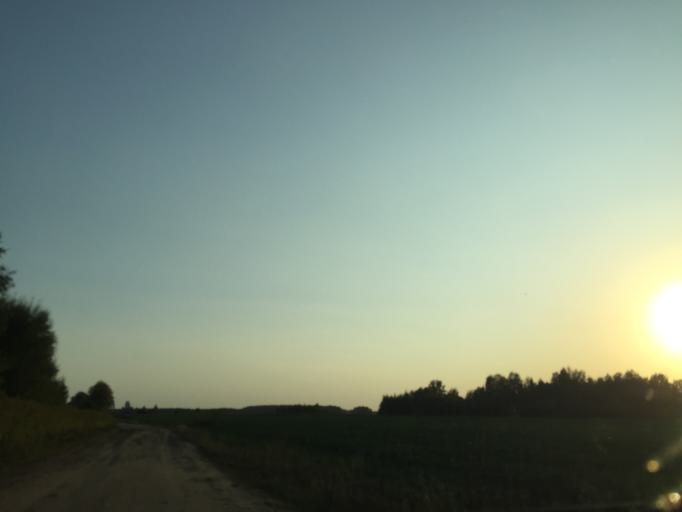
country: LV
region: Lielvarde
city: Lielvarde
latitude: 56.7904
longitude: 24.8175
